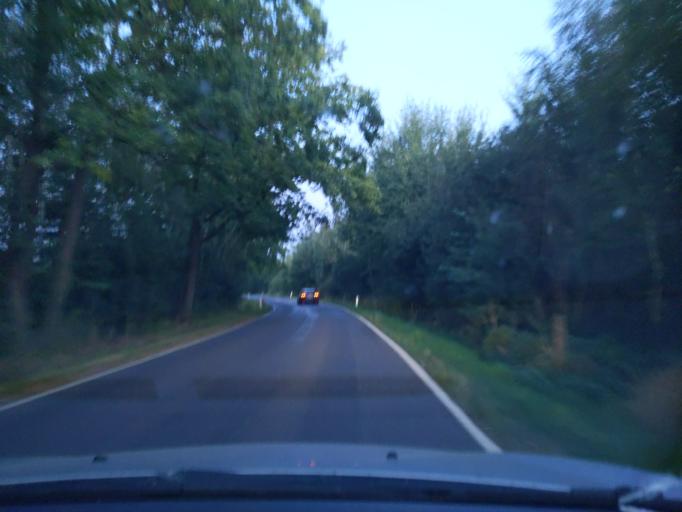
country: DE
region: Saxony
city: Konigswartha
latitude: 51.3449
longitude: 14.3586
